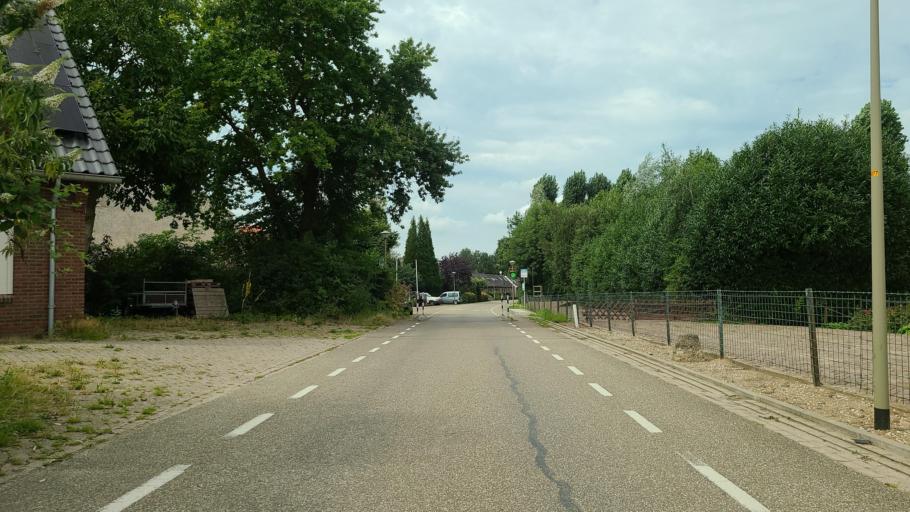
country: NL
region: Gelderland
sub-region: Gemeente Groesbeek
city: Berg en Dal
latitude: 51.8490
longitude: 5.9631
